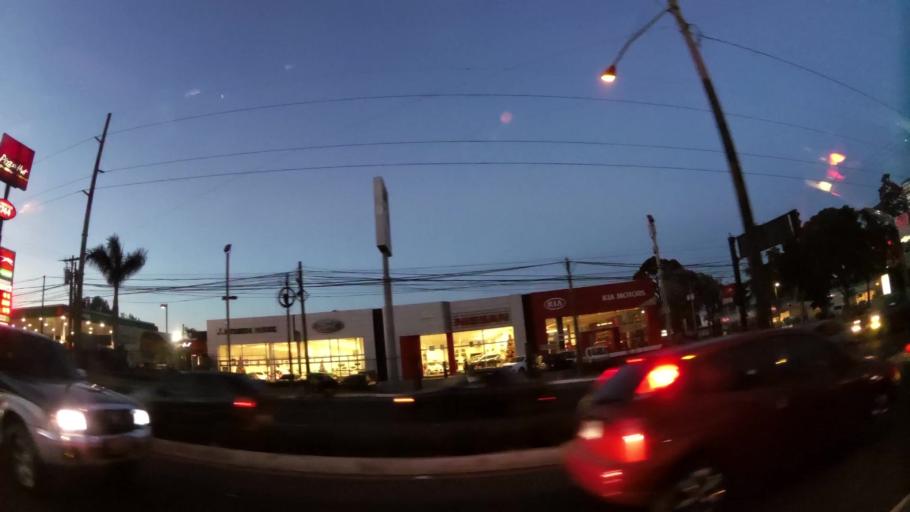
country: GT
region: Guatemala
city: Mixco
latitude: 14.6344
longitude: -90.5845
